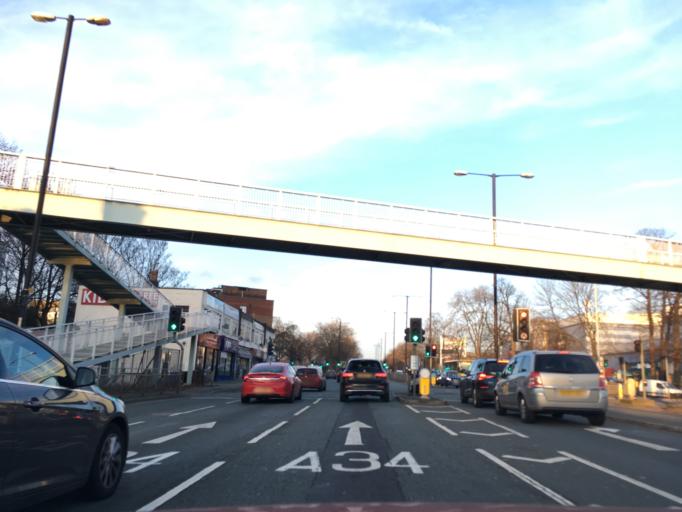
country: GB
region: England
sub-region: Manchester
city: Didsbury
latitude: 53.4084
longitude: -2.2209
